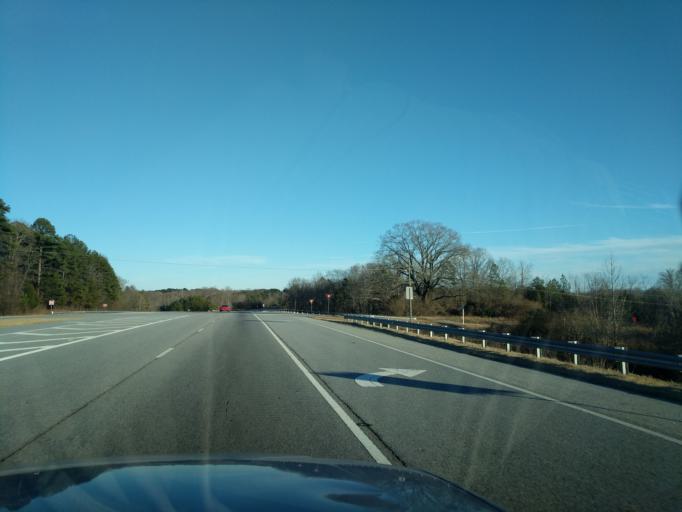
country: US
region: Georgia
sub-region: Stephens County
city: Toccoa
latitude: 34.5384
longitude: -83.3520
